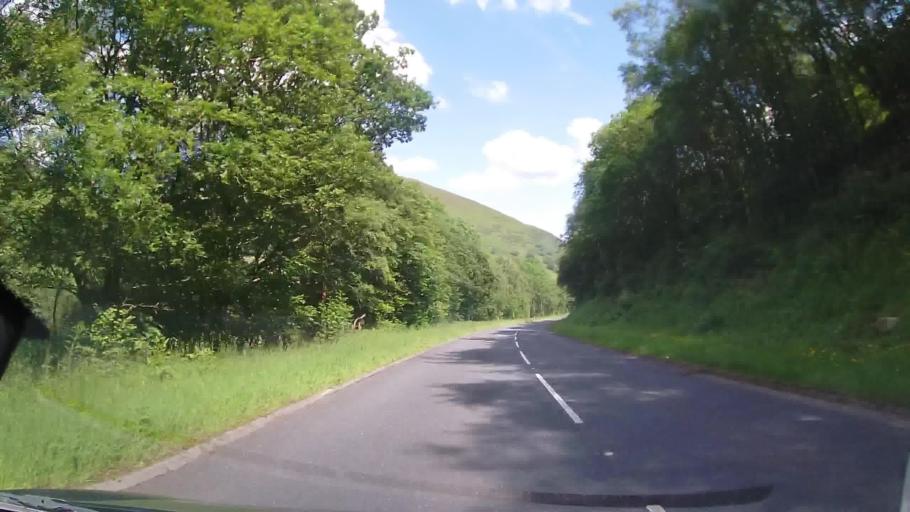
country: GB
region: Wales
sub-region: Gwynedd
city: Corris
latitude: 52.7326
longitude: -3.7234
